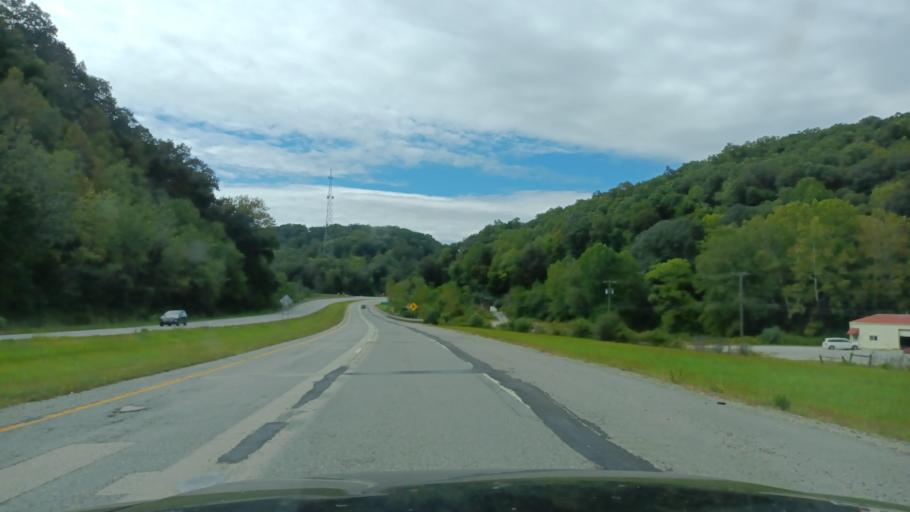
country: US
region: West Virginia
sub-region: Doddridge County
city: West Union
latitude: 39.2779
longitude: -80.8139
